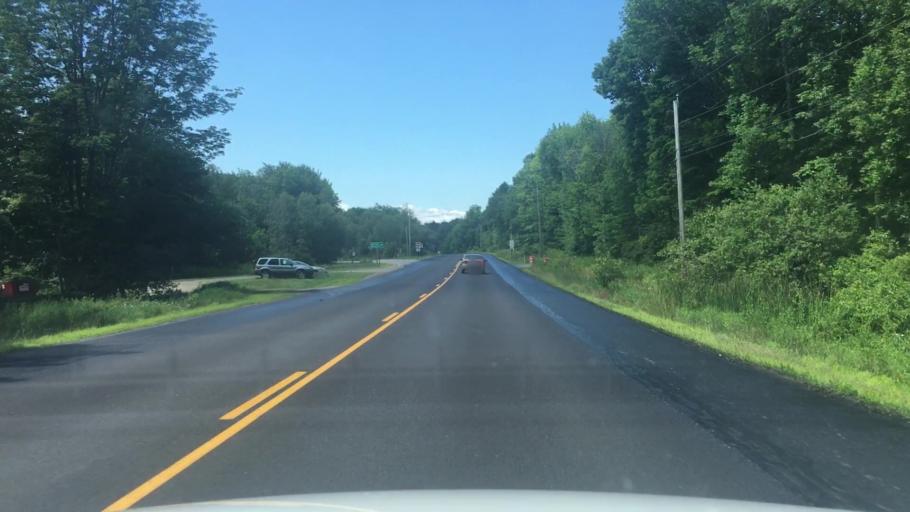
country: US
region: Maine
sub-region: Waldo County
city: Searsmont
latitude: 44.4021
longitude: -69.2679
